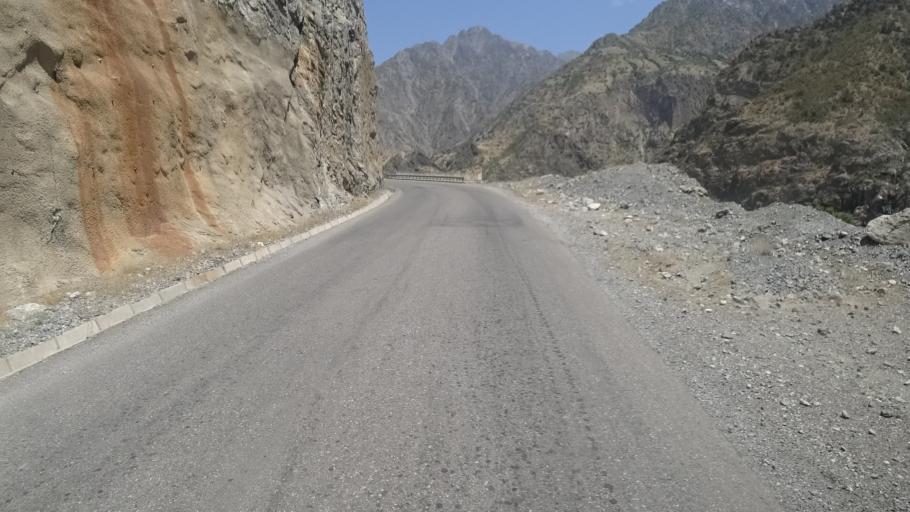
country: AF
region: Badakhshan
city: Qal`ah-ye Kuf
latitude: 37.9975
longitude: 70.3270
